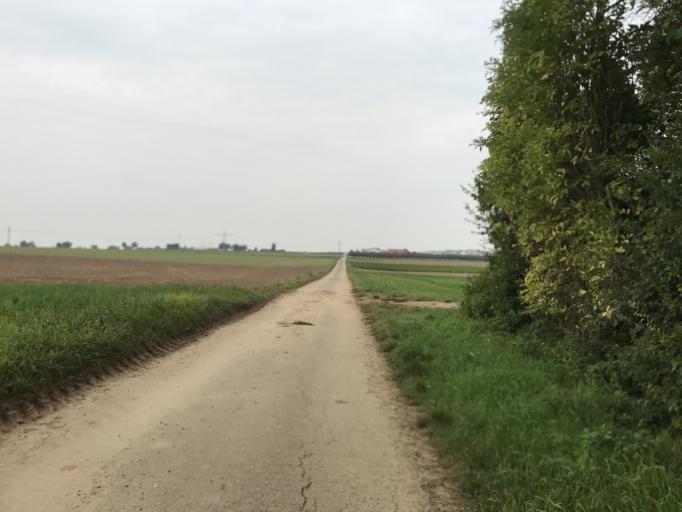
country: DE
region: Rheinland-Pfalz
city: Klein-Winternheim
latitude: 49.9280
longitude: 8.2186
